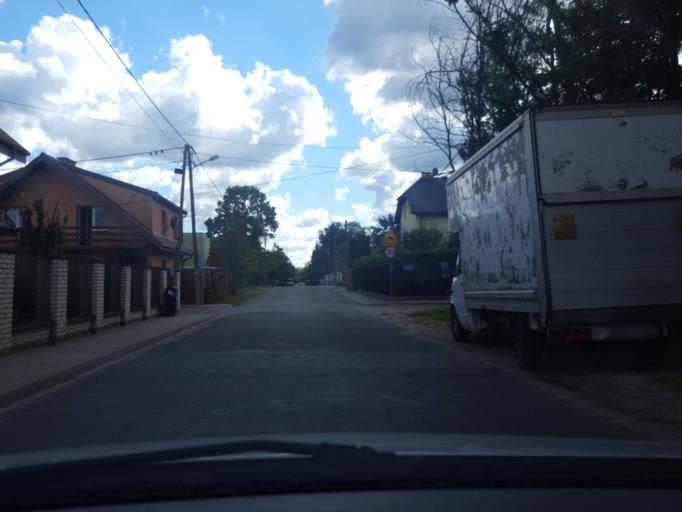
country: PL
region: Masovian Voivodeship
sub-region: Warszawa
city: Rembertow
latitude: 52.2738
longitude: 21.1629
